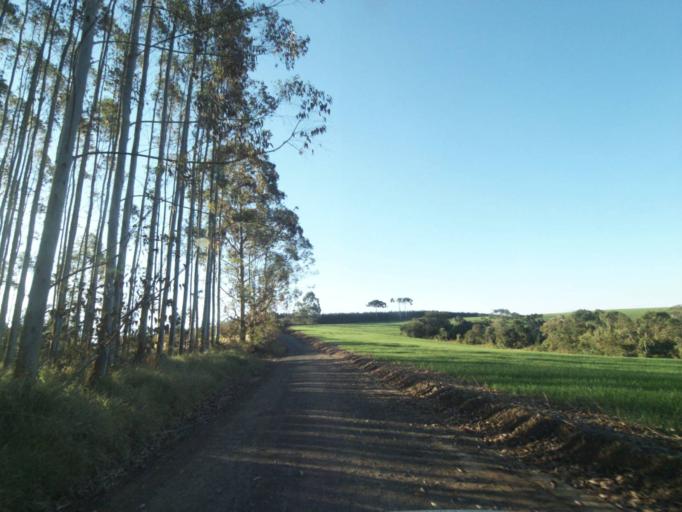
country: BR
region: Parana
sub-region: Telemaco Borba
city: Telemaco Borba
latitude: -24.4362
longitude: -50.6025
